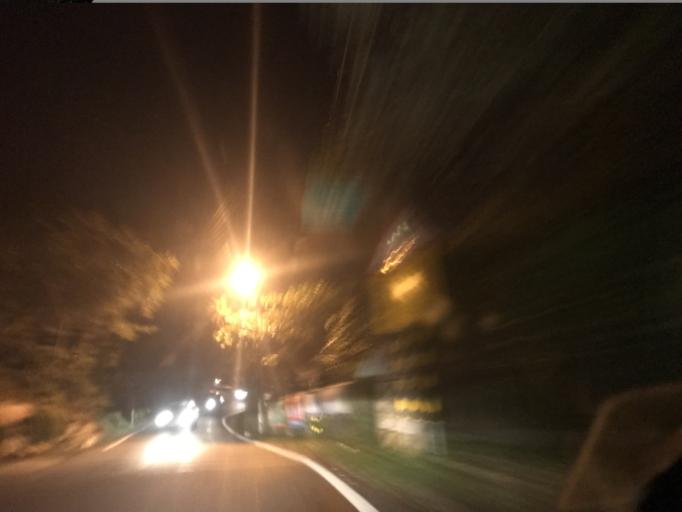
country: TW
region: Taiwan
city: Daxi
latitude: 24.8413
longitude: 121.2135
